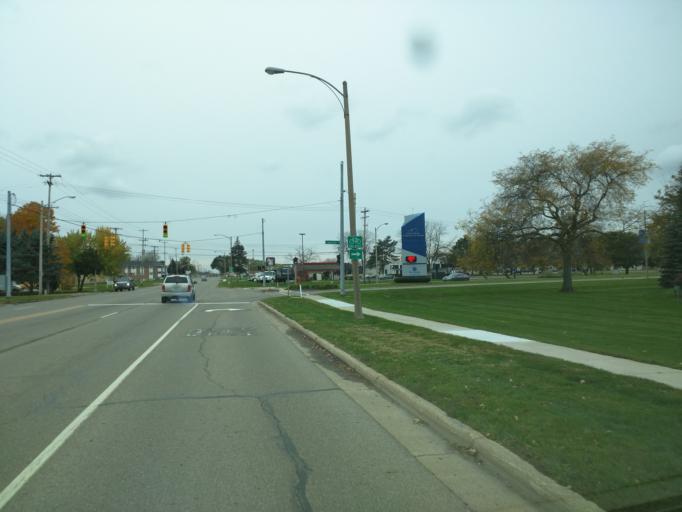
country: US
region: Michigan
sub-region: Ingham County
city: Edgemont Park
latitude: 42.7662
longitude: -84.5883
